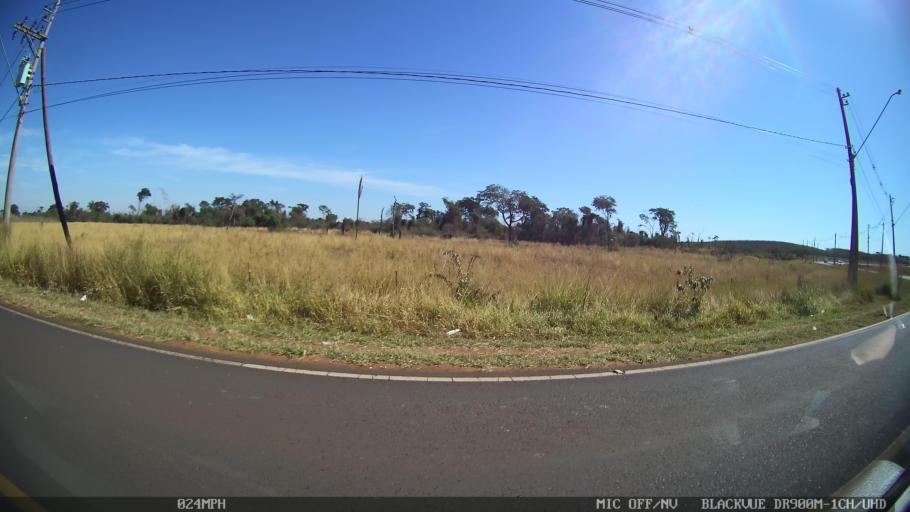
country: BR
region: Sao Paulo
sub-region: Sao Jose Do Rio Preto
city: Sao Jose do Rio Preto
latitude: -20.7445
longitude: -49.4343
